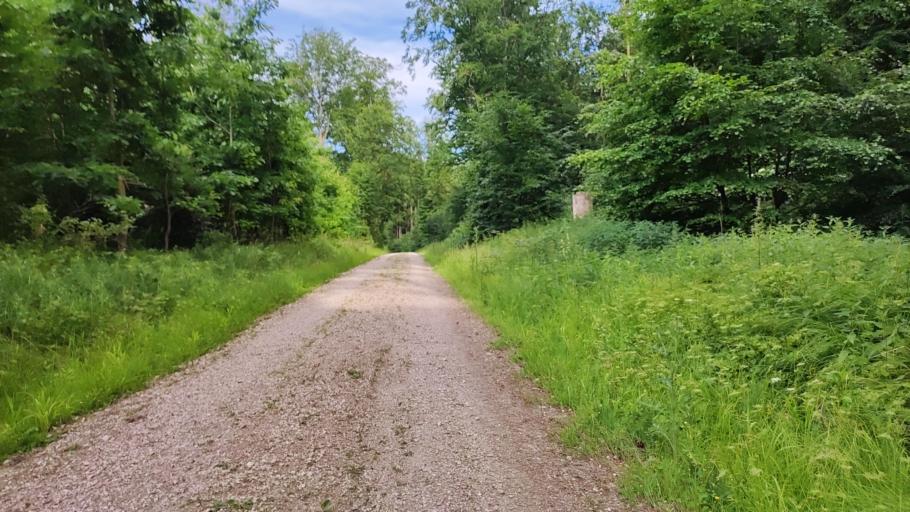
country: DE
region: Bavaria
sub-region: Swabia
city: Landensberg
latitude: 48.4203
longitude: 10.5523
